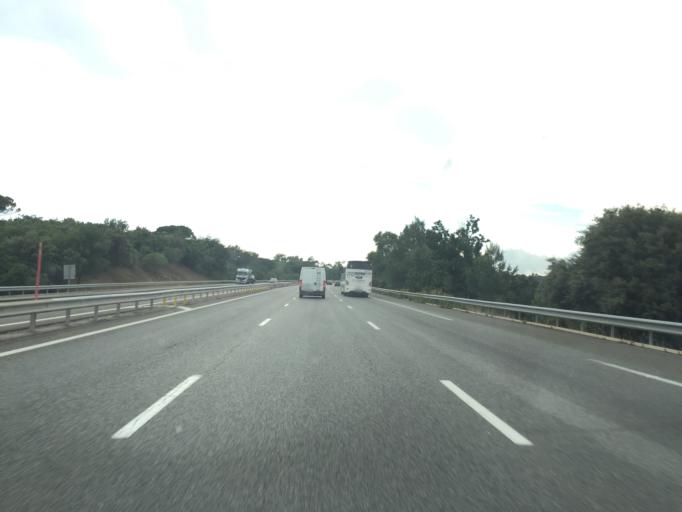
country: FR
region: Provence-Alpes-Cote d'Azur
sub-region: Departement du Var
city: Tourves
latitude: 43.4290
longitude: 5.9439
